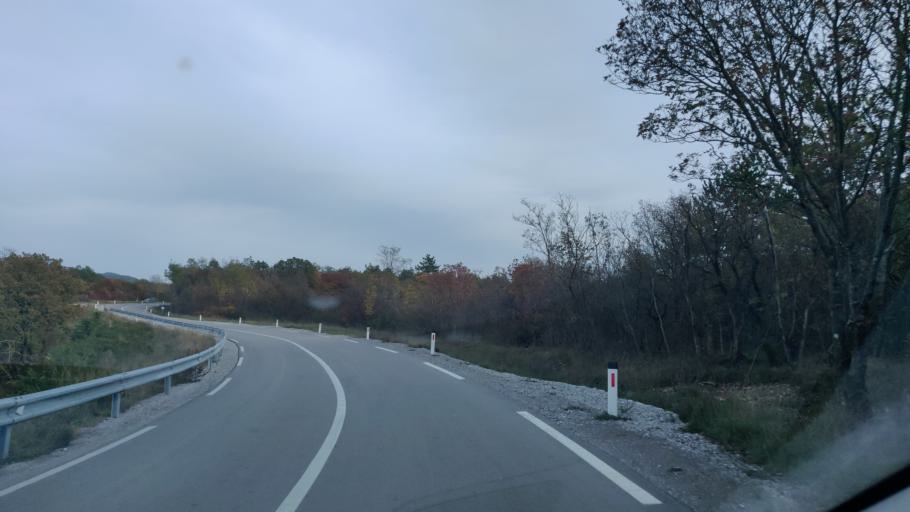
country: SI
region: Miren-Kostanjevica
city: Miren
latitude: 45.8478
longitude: 13.6176
